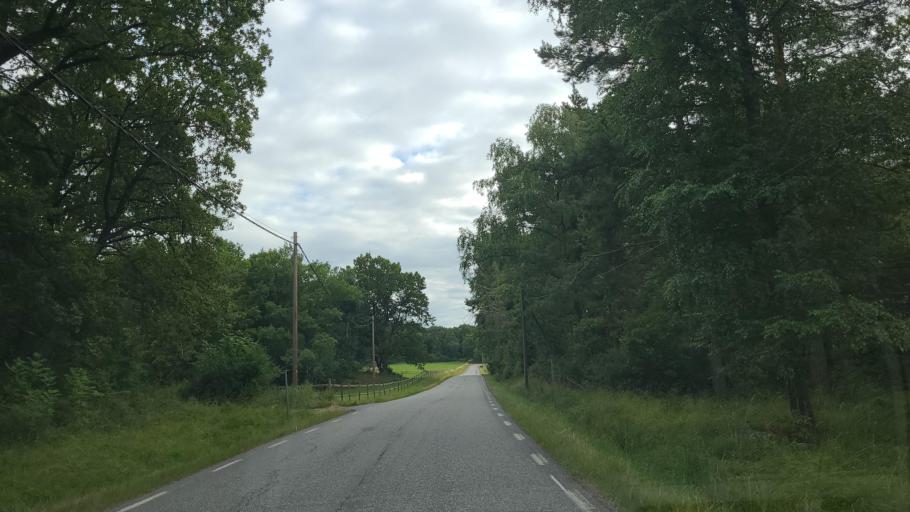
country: SE
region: Stockholm
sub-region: Upplands-Bro Kommun
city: Bro
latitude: 59.4756
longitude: 17.5965
